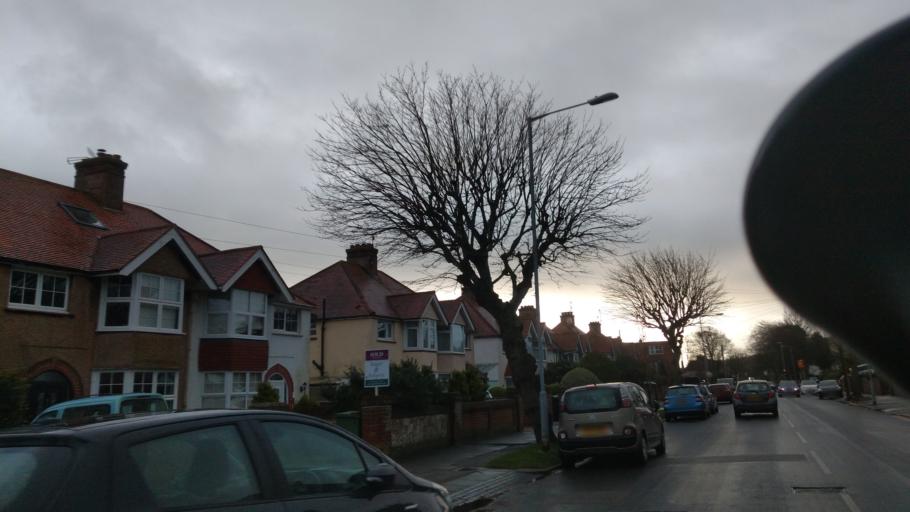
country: GB
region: England
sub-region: East Sussex
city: Eastbourne
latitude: 50.7792
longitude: 0.2554
